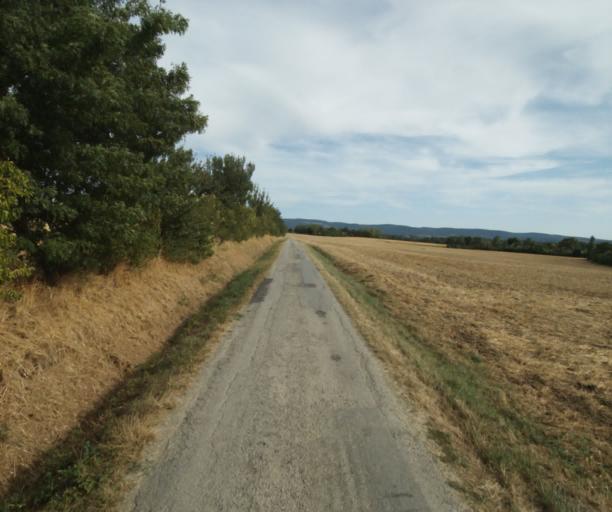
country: FR
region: Midi-Pyrenees
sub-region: Departement du Tarn
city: Puylaurens
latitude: 43.5290
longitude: 2.0371
